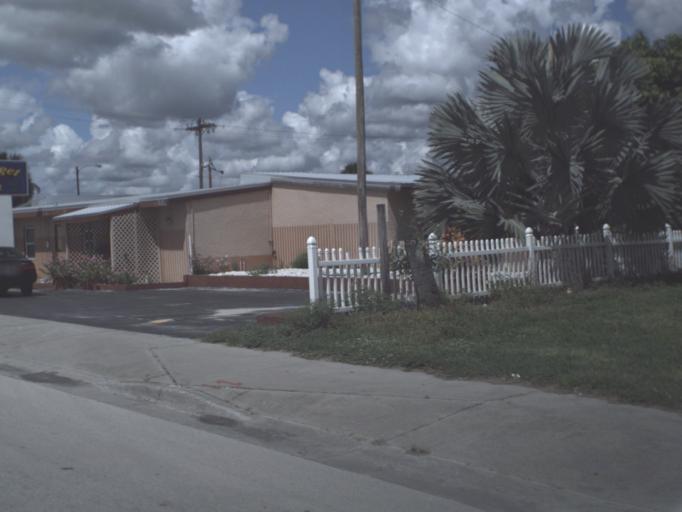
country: US
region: Florida
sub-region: Collier County
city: Immokalee
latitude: 26.4186
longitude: -81.4113
